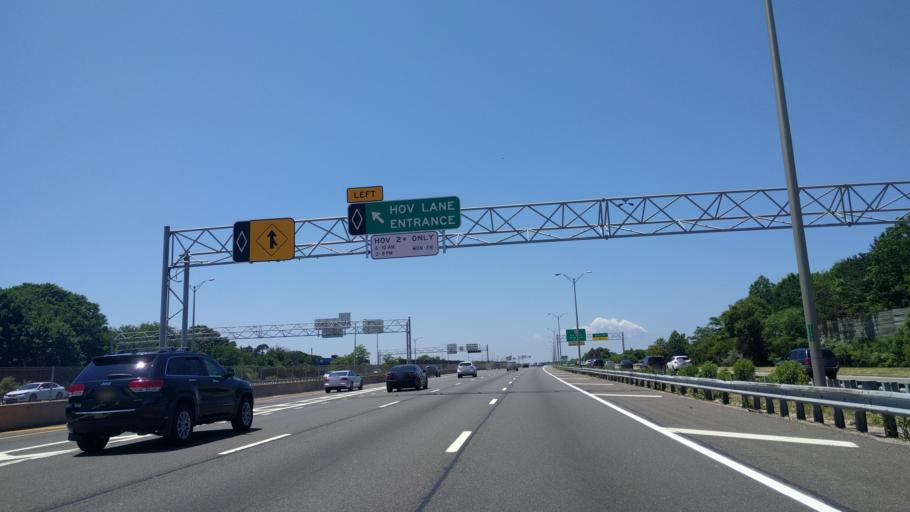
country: US
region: New York
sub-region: Suffolk County
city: Brentwood
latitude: 40.8049
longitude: -73.2627
